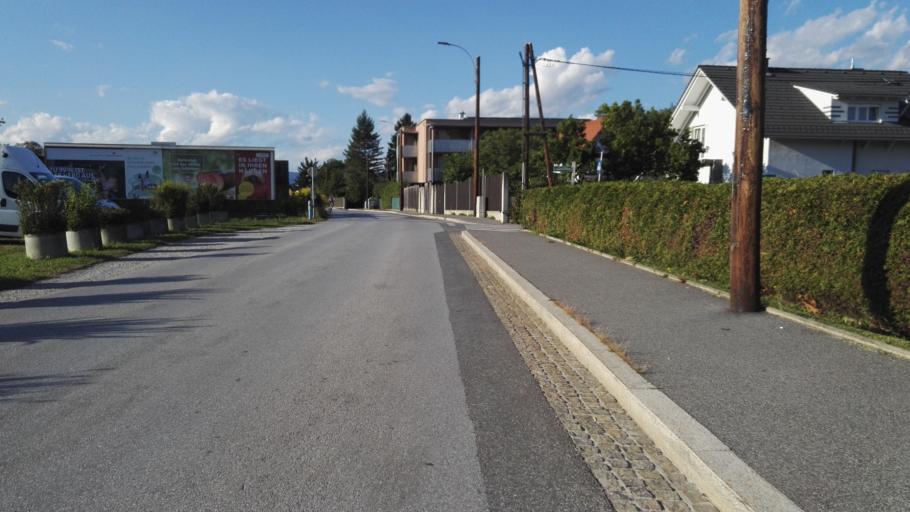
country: AT
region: Styria
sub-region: Politischer Bezirk Graz-Umgebung
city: Feldkirchen bei Graz
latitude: 47.0363
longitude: 15.4336
